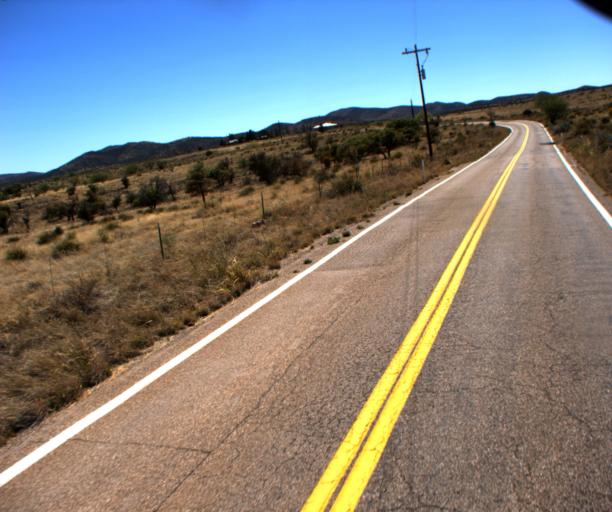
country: US
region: Arizona
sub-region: Cochise County
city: Huachuca City
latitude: 31.5878
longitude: -110.5618
